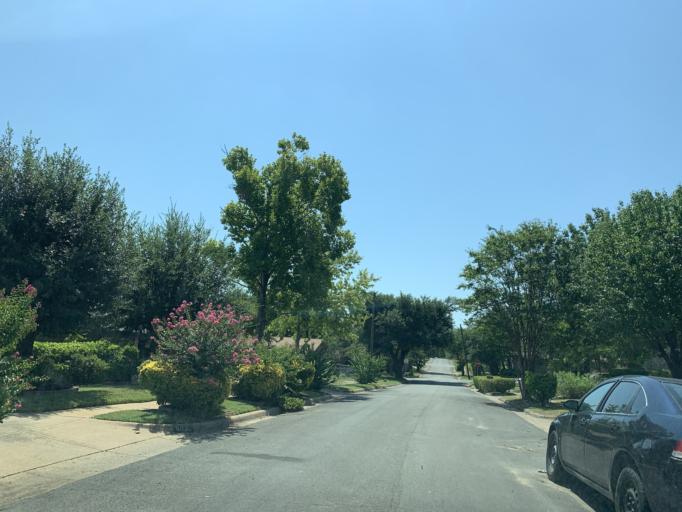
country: US
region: Texas
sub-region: Dallas County
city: Hutchins
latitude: 32.6755
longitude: -96.7521
